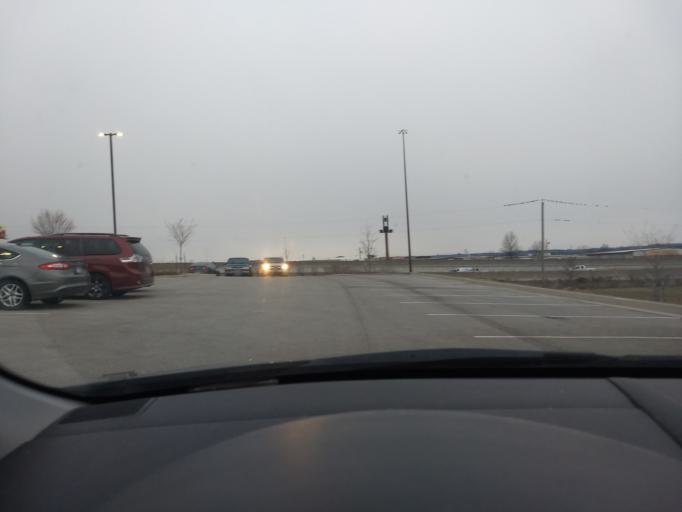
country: US
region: Indiana
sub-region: Clark County
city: Clarksville
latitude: 38.3311
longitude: -85.7527
